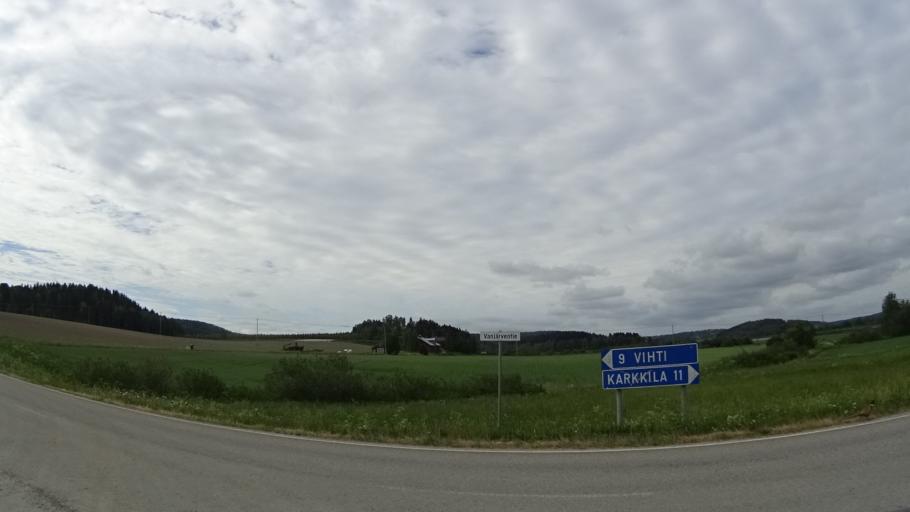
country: FI
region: Uusimaa
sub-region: Helsinki
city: Karkkila
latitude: 60.4555
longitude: 24.2386
